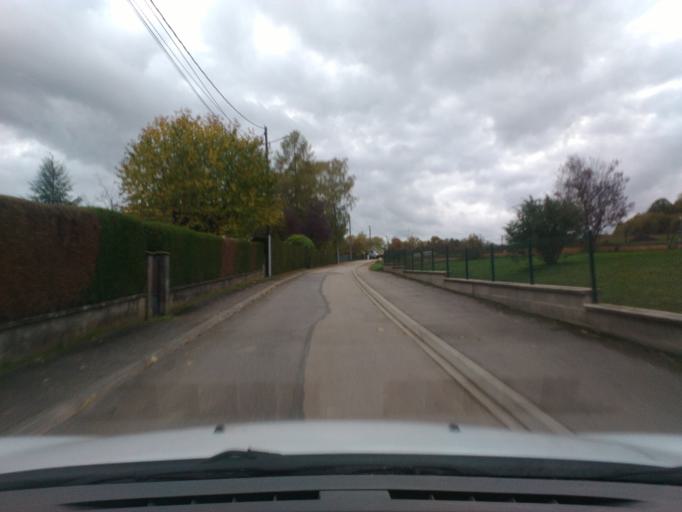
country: FR
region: Lorraine
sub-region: Departement des Vosges
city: Mirecourt
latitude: 48.3428
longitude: 6.1374
